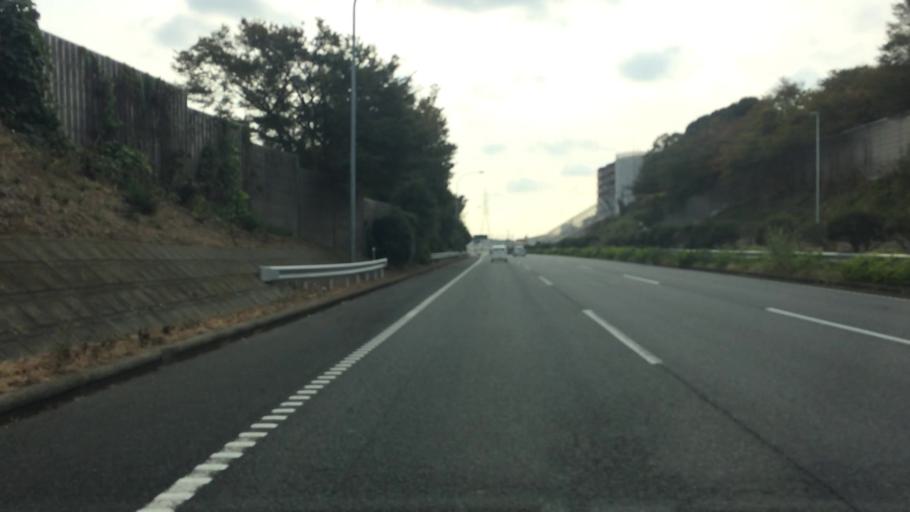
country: JP
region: Tokyo
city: Chofugaoka
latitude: 35.5685
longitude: 139.6130
